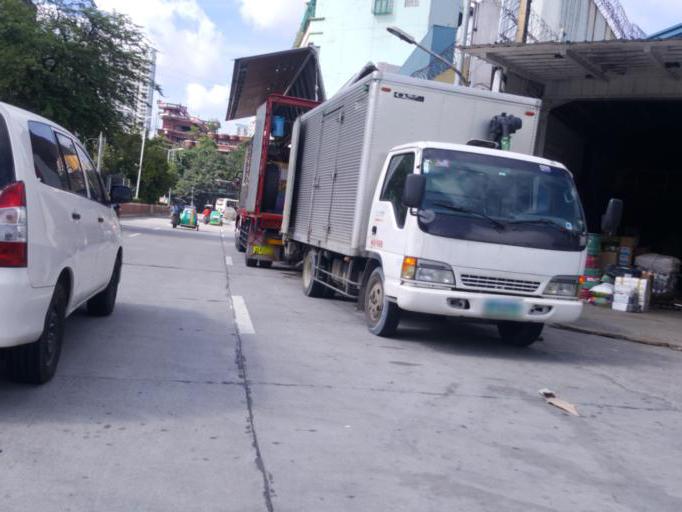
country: PH
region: Metro Manila
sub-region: City of Manila
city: Manila
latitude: 14.6148
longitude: 120.9866
